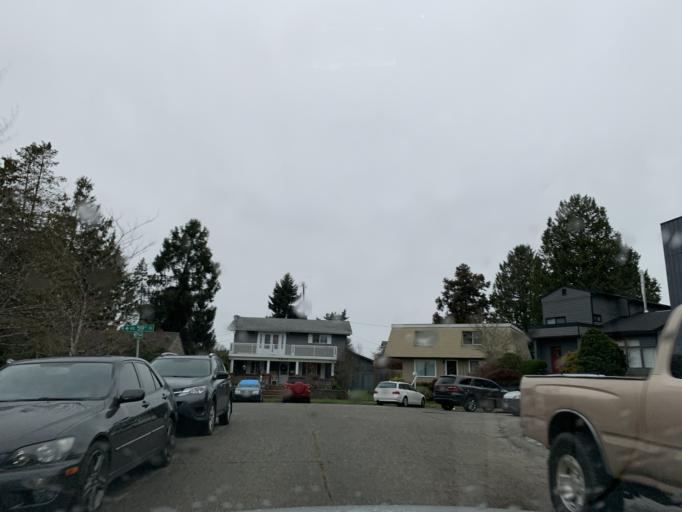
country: US
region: Washington
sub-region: King County
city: Yarrow Point
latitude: 47.6714
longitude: -122.2668
